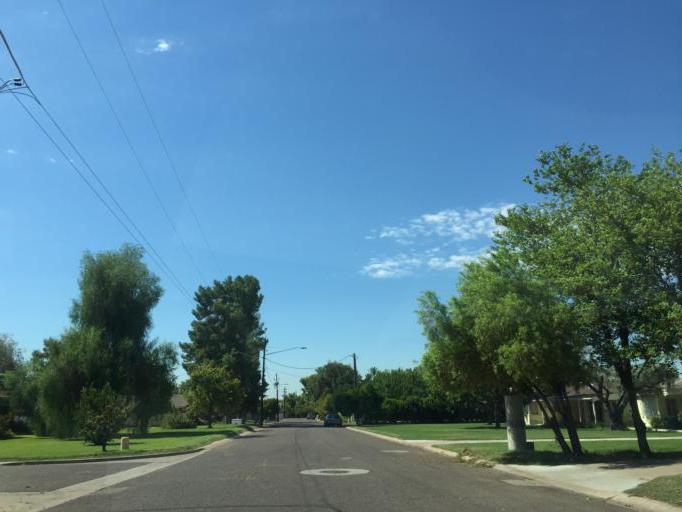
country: US
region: Arizona
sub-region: Maricopa County
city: Phoenix
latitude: 33.5330
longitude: -112.0518
